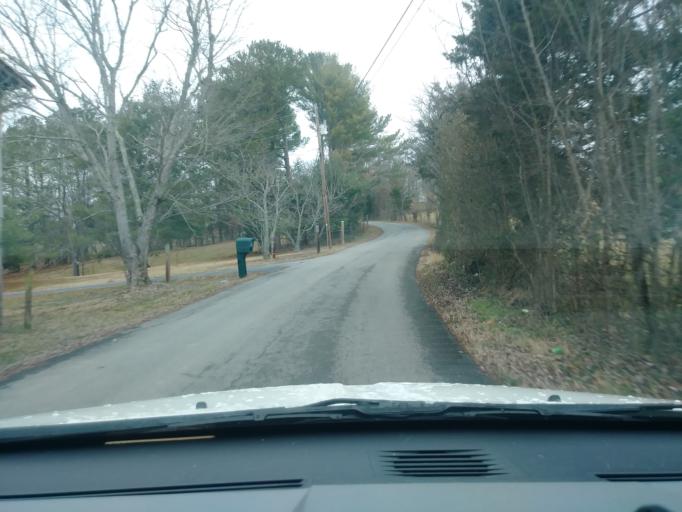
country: US
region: Tennessee
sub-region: Greene County
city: Greeneville
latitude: 36.1008
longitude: -82.8843
